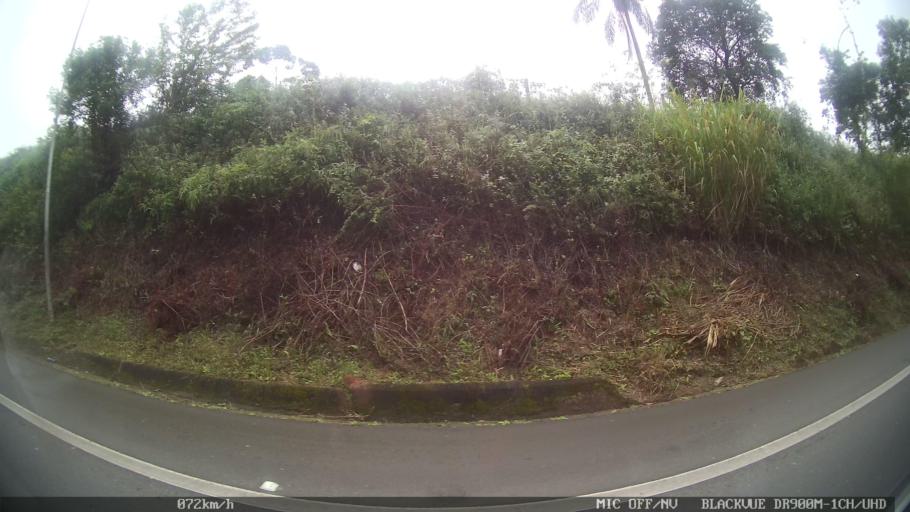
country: BR
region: Santa Catarina
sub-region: Joinville
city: Joinville
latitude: -26.3847
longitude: -48.8444
